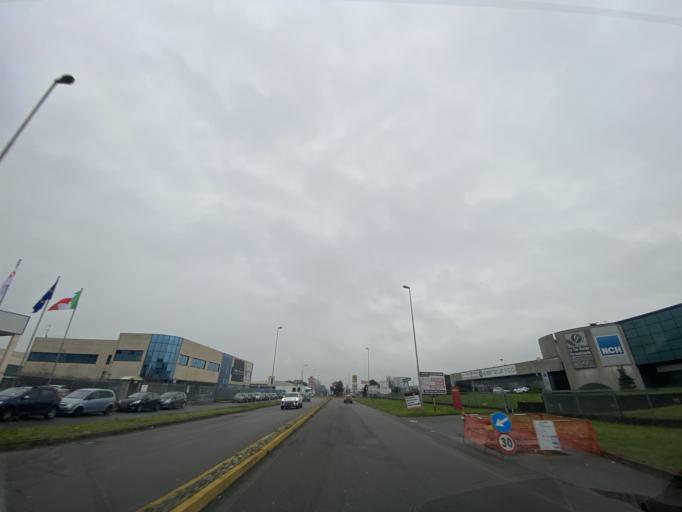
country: IT
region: Lombardy
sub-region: Citta metropolitana di Milano
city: Cusago
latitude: 45.4437
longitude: 9.0408
